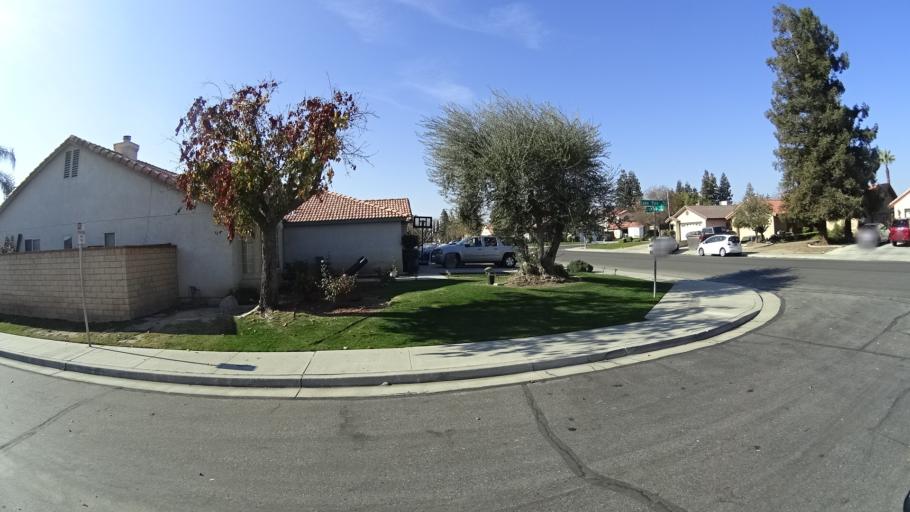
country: US
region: California
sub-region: Kern County
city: Greenacres
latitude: 35.3211
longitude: -119.1145
